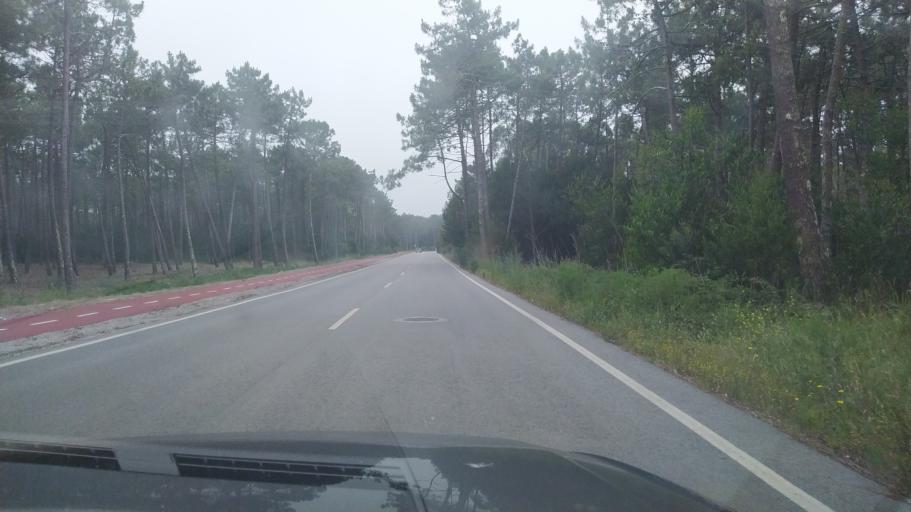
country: PT
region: Aveiro
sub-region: Ilhavo
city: Gafanha da Encarnacao
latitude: 40.5755
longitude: -8.7349
